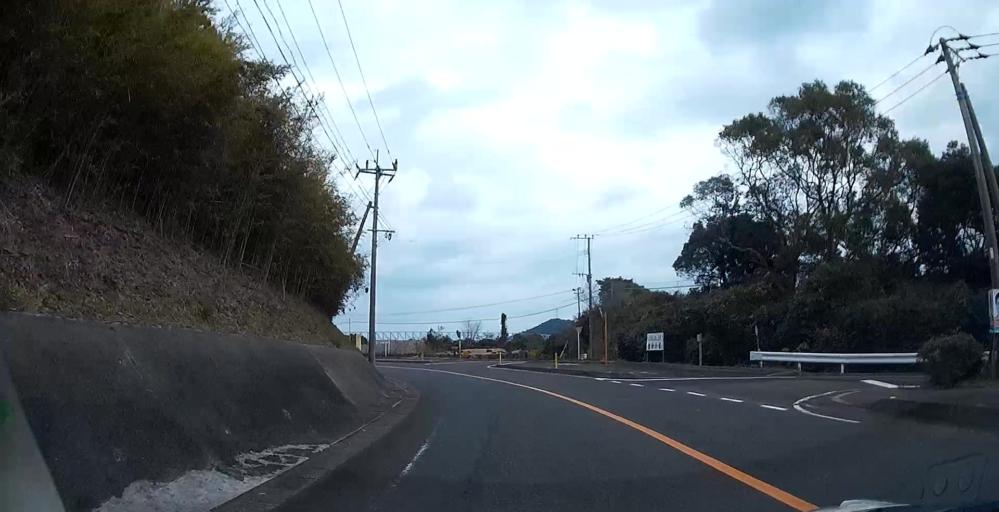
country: JP
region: Kagoshima
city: Akune
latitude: 32.0999
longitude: 130.1673
